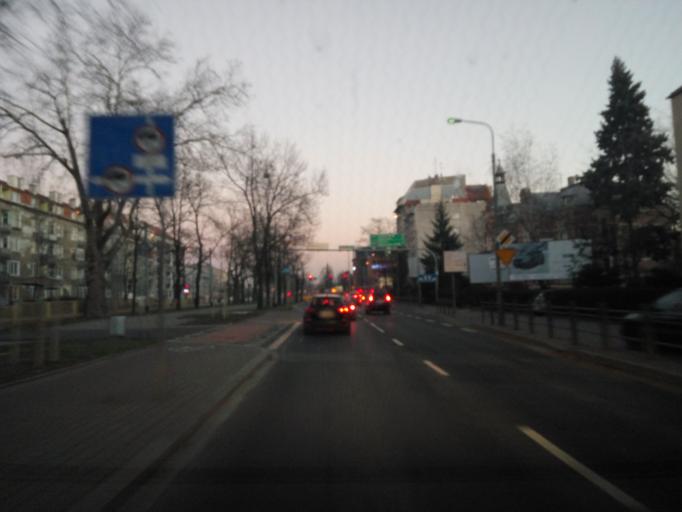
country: PL
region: Lower Silesian Voivodeship
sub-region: Powiat wroclawski
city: Wroclaw
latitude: 51.0870
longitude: 17.0095
